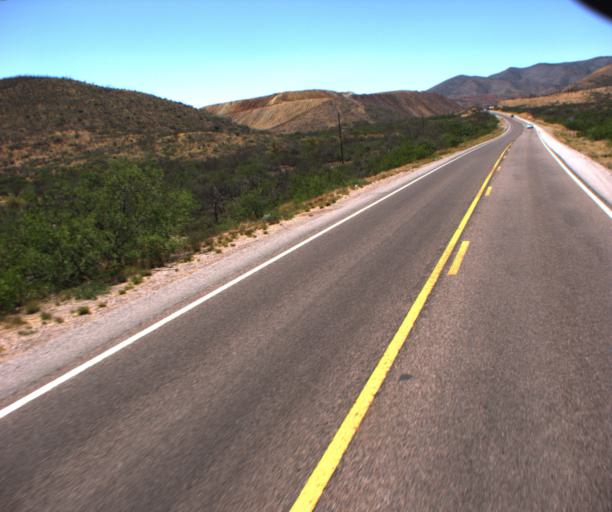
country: US
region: Arizona
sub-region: Cochise County
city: Bisbee
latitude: 31.4311
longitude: -109.8571
